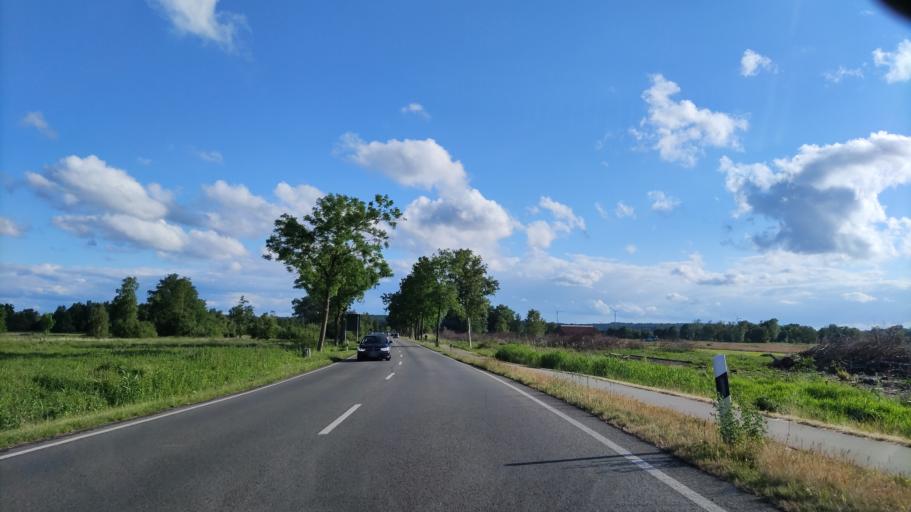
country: DE
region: Lower Saxony
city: Jork
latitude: 53.4981
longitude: 9.6566
